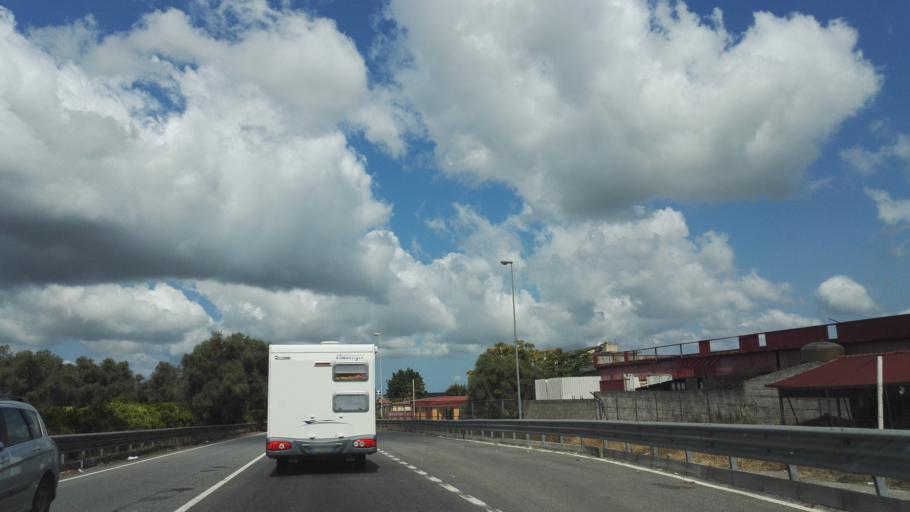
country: IT
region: Calabria
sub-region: Provincia di Reggio Calabria
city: Melicucco
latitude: 38.4532
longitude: 16.0281
